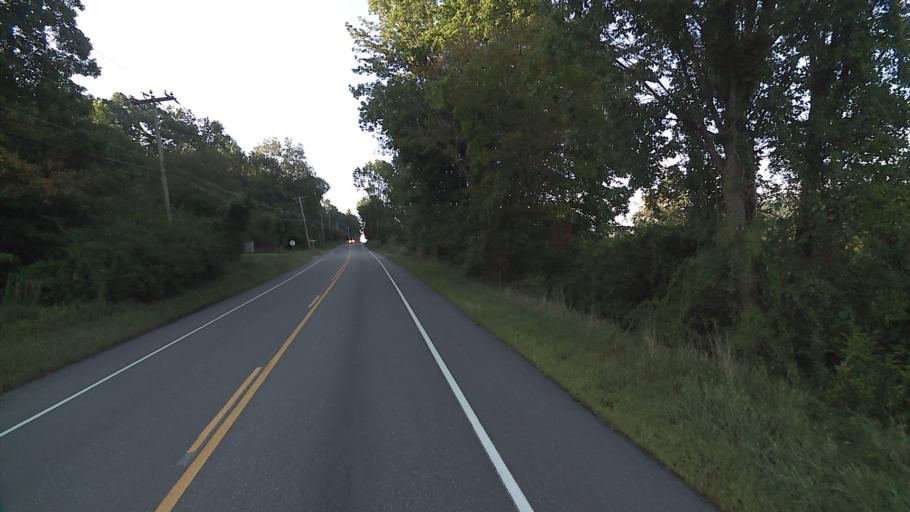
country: US
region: Connecticut
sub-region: Tolland County
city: South Coventry
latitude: 41.8177
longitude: -72.3098
